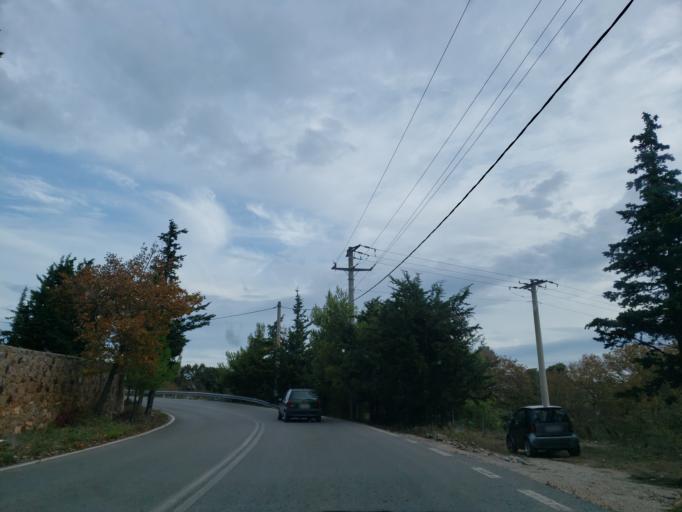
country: GR
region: Attica
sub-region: Nomarchia Anatolikis Attikis
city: Varnavas
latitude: 38.2193
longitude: 23.9359
